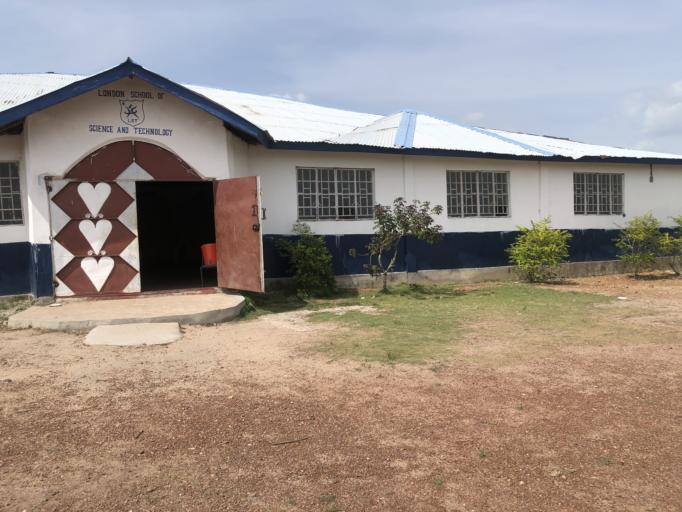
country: SL
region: Northern Province
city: Yonibana
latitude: 8.4720
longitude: -12.2327
